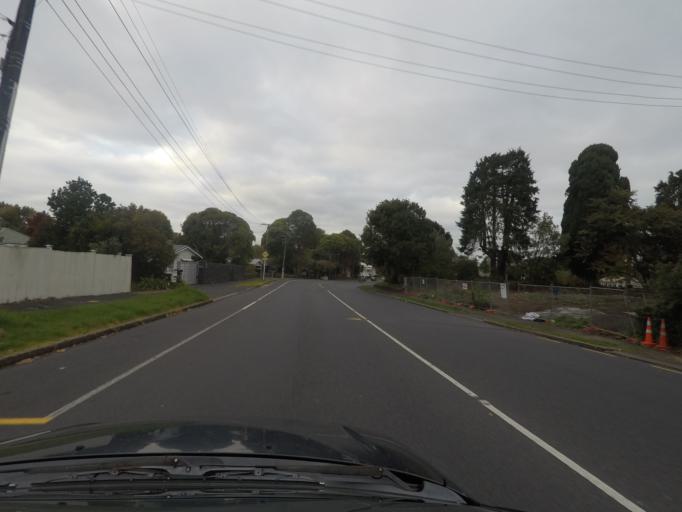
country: NZ
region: Auckland
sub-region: Auckland
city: Auckland
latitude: -36.8848
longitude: 174.7711
